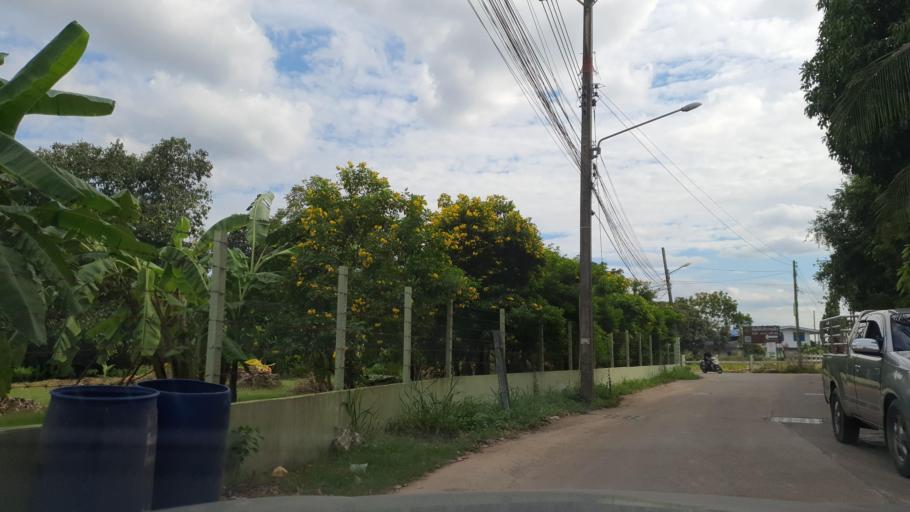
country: TH
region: Chon Buri
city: Phatthaya
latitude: 12.9560
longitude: 100.9153
